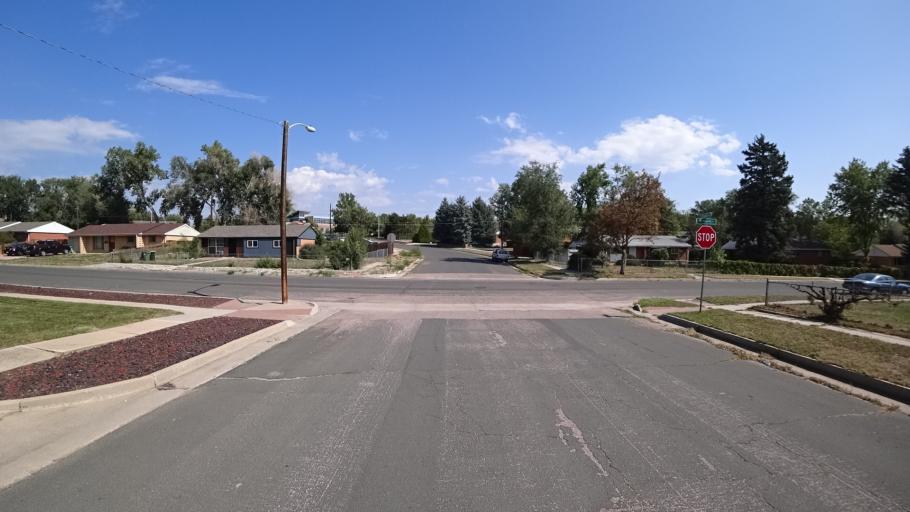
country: US
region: Colorado
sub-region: El Paso County
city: Colorado Springs
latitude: 38.8242
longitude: -104.7885
